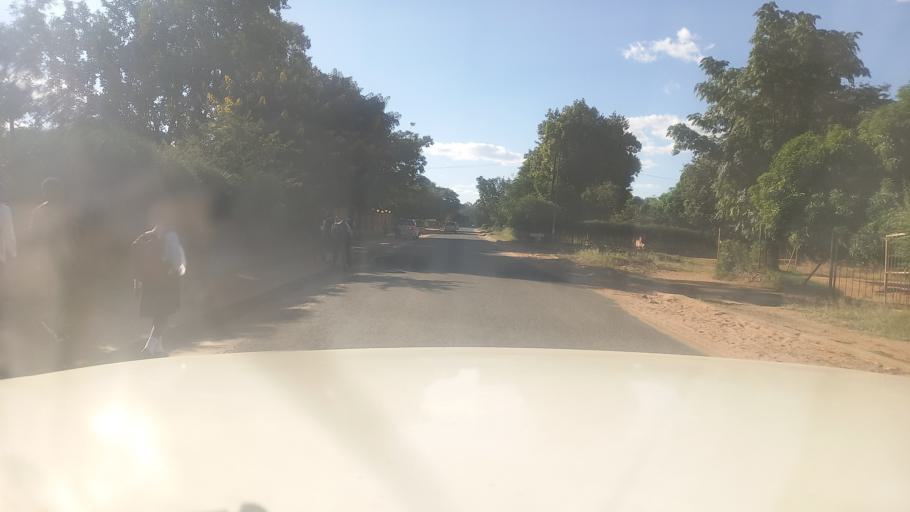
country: ZM
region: Southern
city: Livingstone
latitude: -17.8357
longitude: 25.8659
